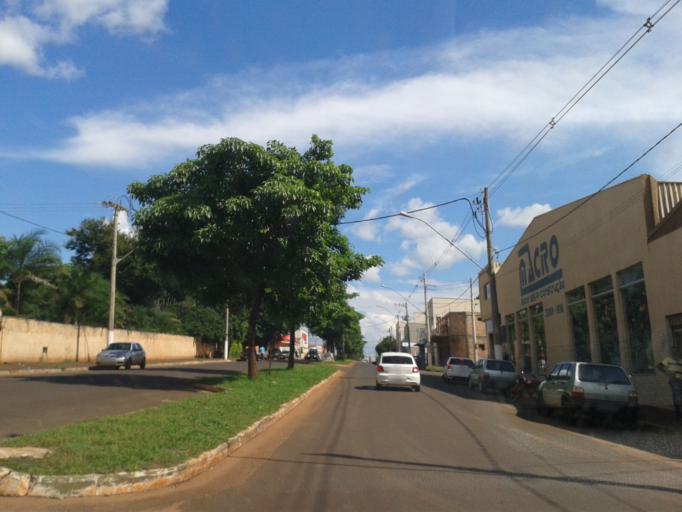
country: BR
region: Minas Gerais
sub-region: Ituiutaba
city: Ituiutaba
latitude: -18.9772
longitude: -49.4821
